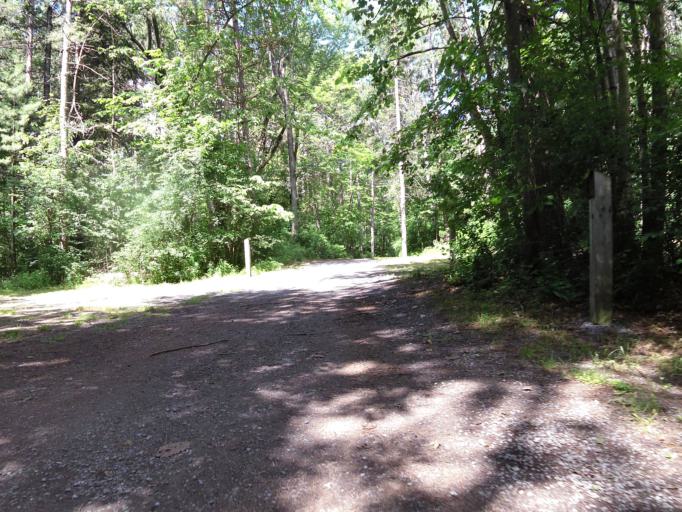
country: CA
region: Ontario
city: Arnprior
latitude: 45.4817
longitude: -76.2247
